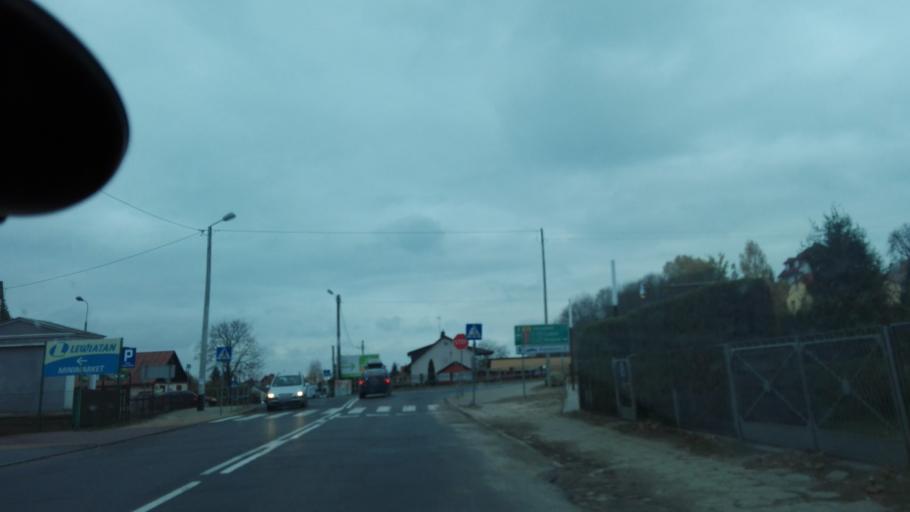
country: PL
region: Lublin Voivodeship
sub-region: Powiat pulawski
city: Pulawy
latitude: 51.4106
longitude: 21.9331
